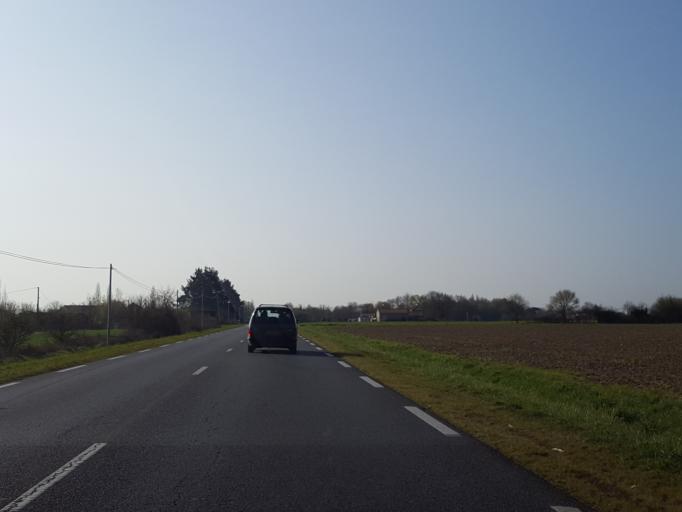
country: FR
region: Pays de la Loire
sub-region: Departement de la Loire-Atlantique
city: Le Bignon
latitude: 47.1014
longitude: -1.5347
